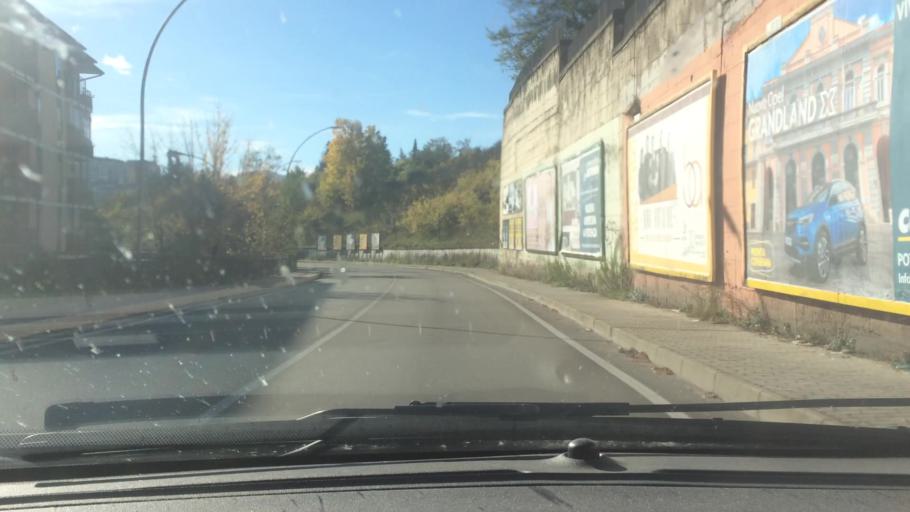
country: IT
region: Basilicate
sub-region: Provincia di Potenza
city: Potenza
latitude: 40.6440
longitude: 15.7960
